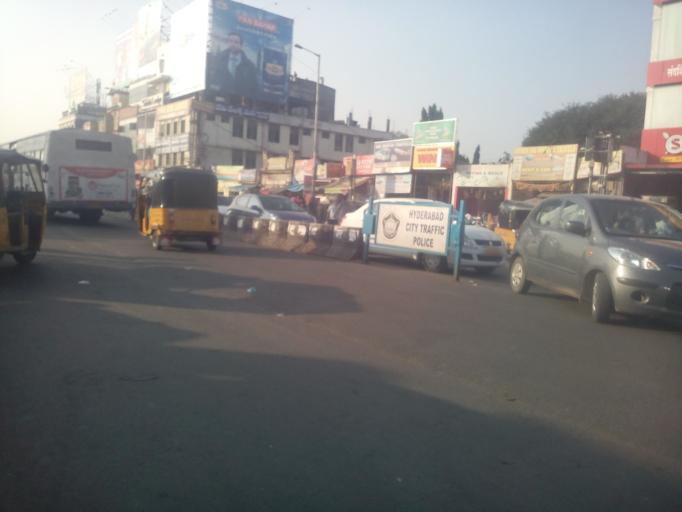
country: IN
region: Telangana
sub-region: Hyderabad
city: Malkajgiri
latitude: 17.4344
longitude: 78.5024
